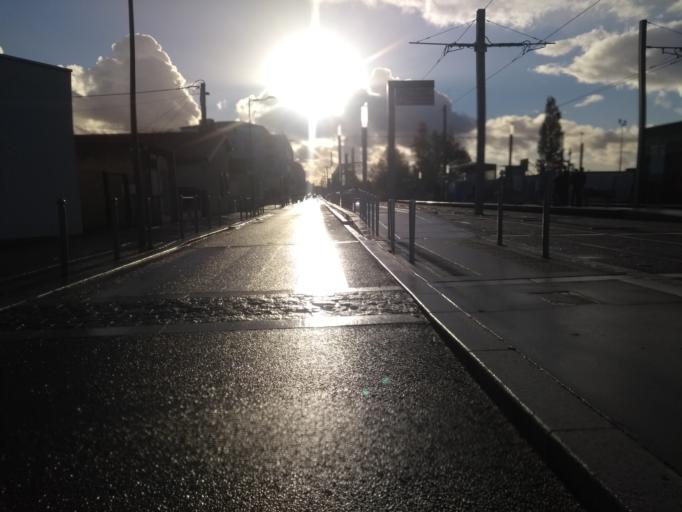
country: FR
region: Aquitaine
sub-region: Departement de la Gironde
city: Begles
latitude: 44.8201
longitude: -0.5500
